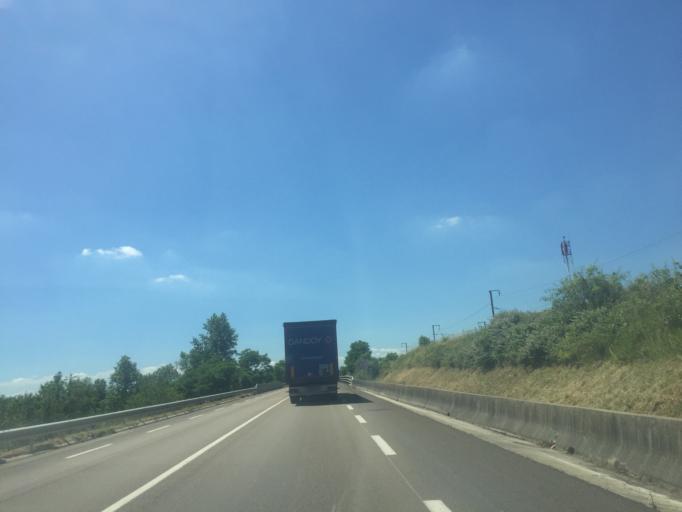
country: FR
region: Rhone-Alpes
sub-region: Departement du Rhone
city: Pusignan
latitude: 45.7613
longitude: 5.0831
